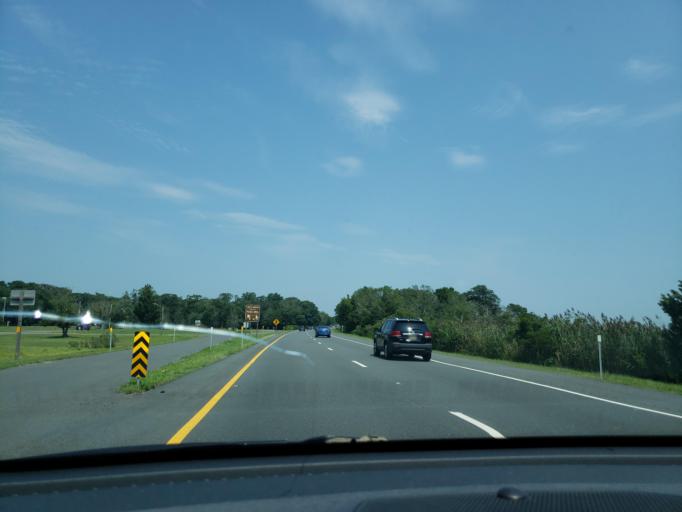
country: US
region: New Jersey
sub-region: Cape May County
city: Sea Isle City
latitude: 39.2308
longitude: -74.6726
